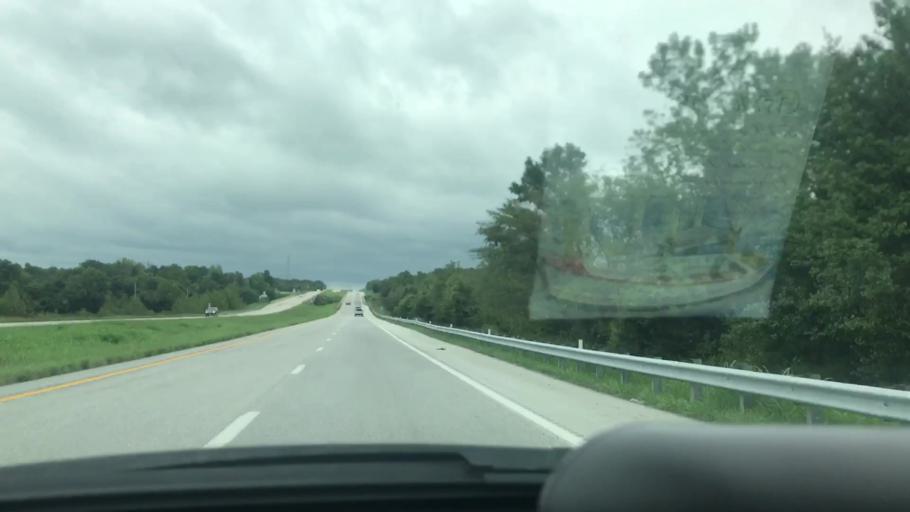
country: US
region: Missouri
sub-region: Greene County
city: Fair Grove
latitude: 37.4122
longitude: -93.1452
